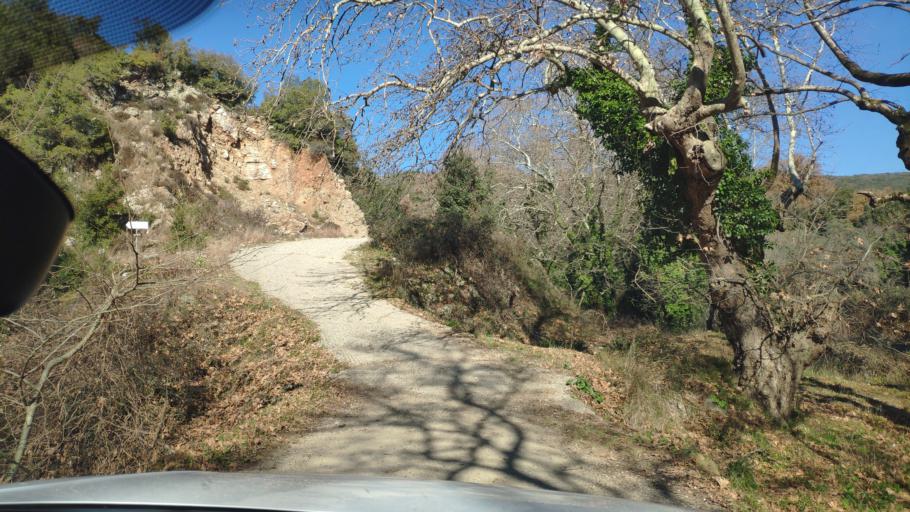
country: GR
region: West Greece
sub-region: Nomos Aitolias kai Akarnanias
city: Thermo
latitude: 38.5799
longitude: 21.6329
